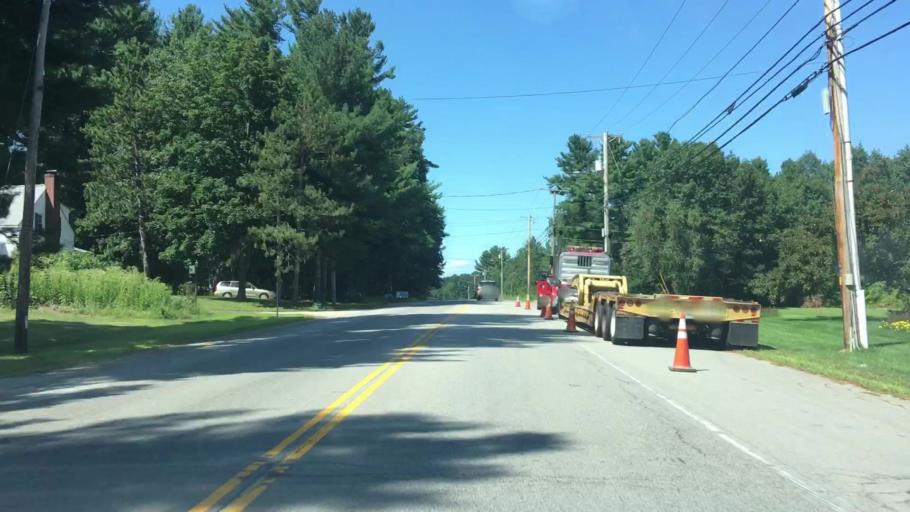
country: US
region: Maine
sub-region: York County
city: Eliot
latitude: 43.1550
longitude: -70.8408
